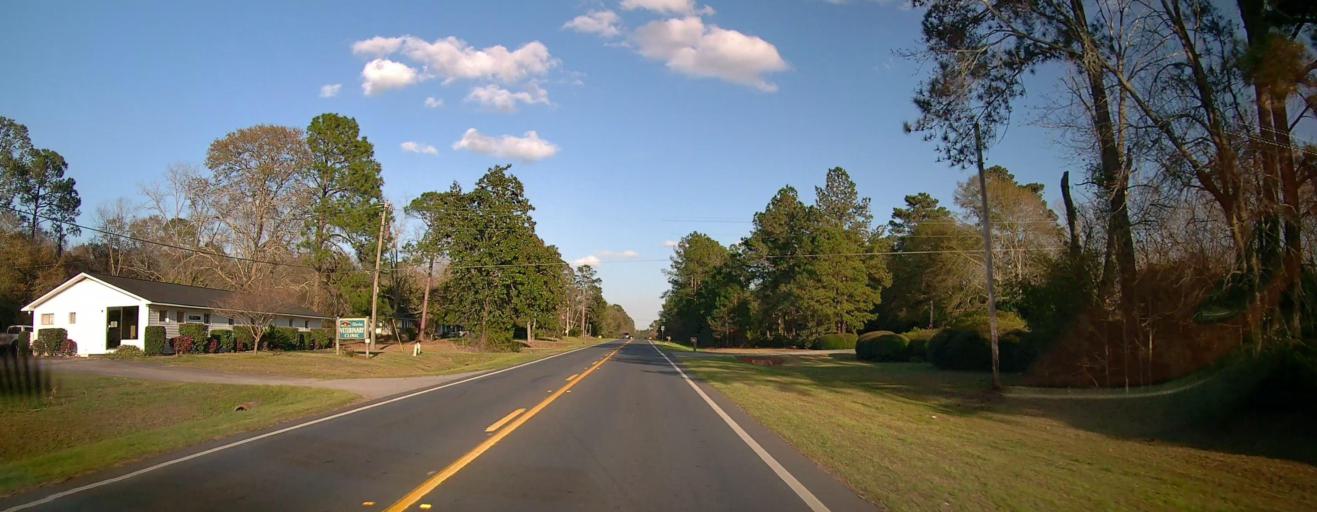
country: US
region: Georgia
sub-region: Evans County
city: Claxton
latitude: 32.1615
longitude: -81.8920
